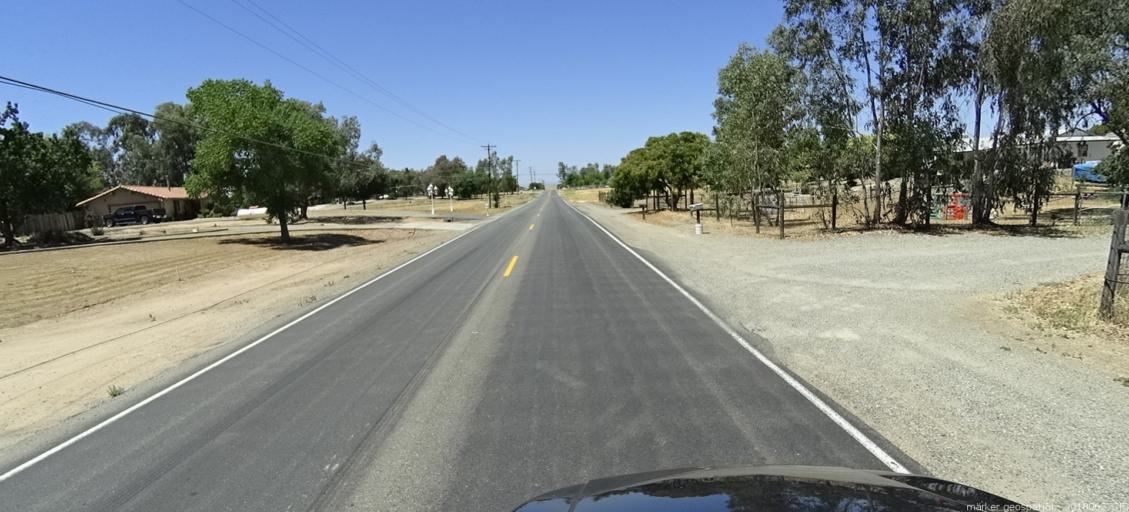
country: US
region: California
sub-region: Madera County
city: Bonadelle Ranchos-Madera Ranchos
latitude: 36.9604
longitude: -119.9120
